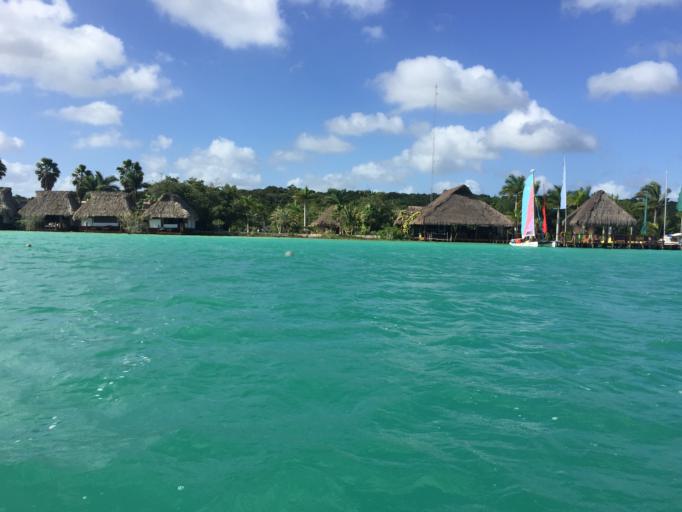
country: MX
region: Quintana Roo
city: Bacalar
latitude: 18.6236
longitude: -88.4155
